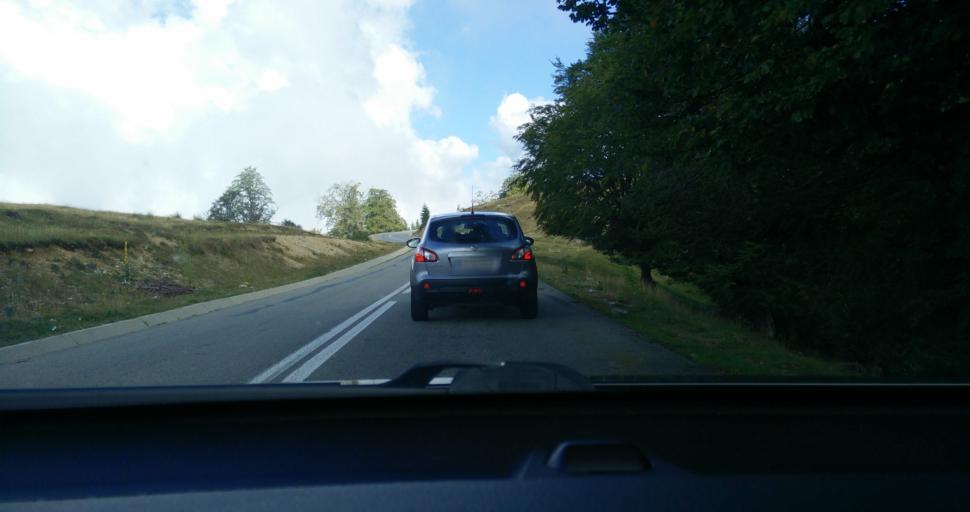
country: RO
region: Gorj
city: Novaci-Straini
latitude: 45.2307
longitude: 23.6879
